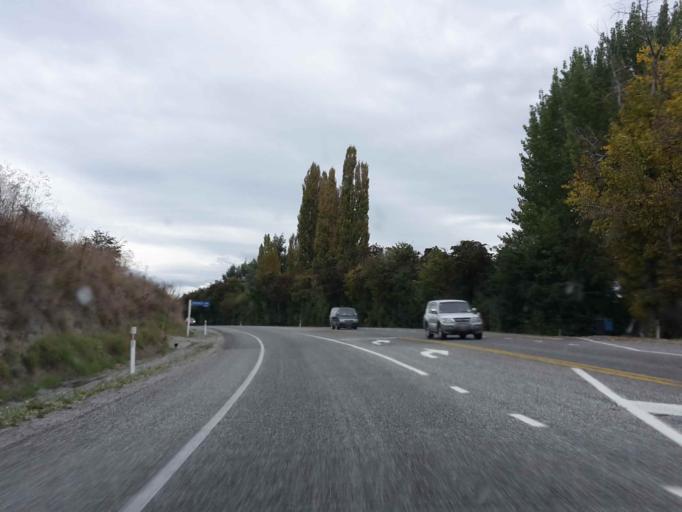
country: NZ
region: Otago
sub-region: Queenstown-Lakes District
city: Arrowtown
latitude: -44.9793
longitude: 168.8277
